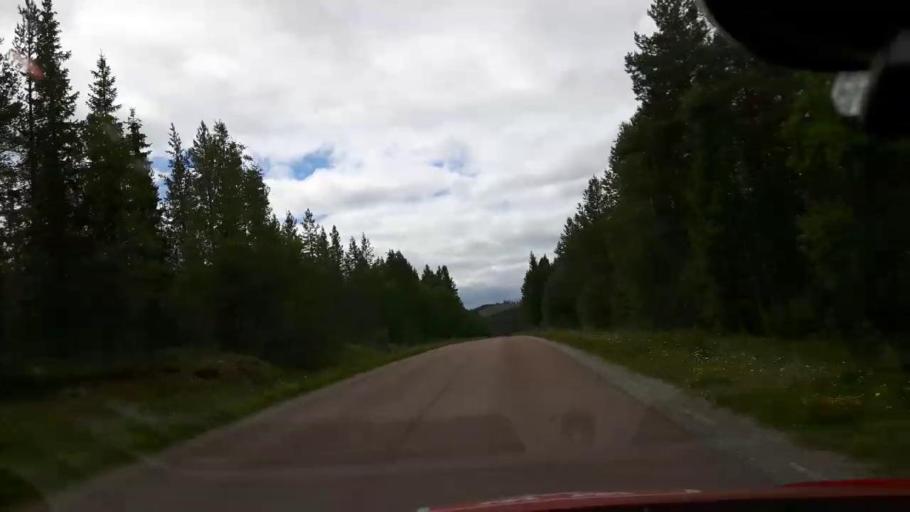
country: SE
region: Jaemtland
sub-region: Braecke Kommun
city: Braecke
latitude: 62.9047
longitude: 15.1495
